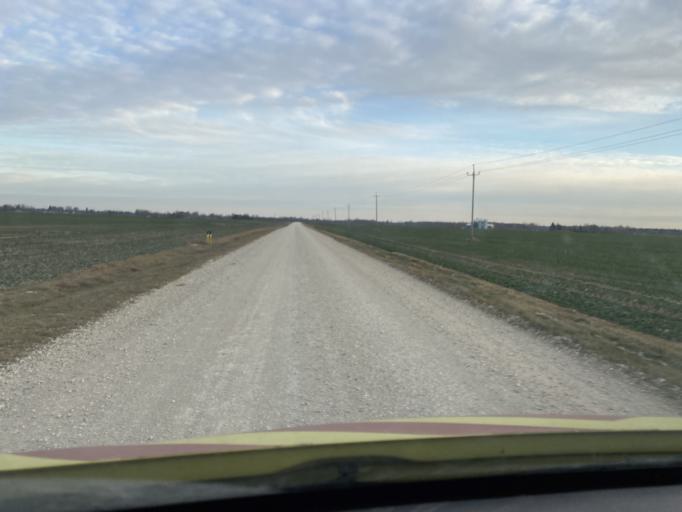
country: EE
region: Jogevamaa
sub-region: Poltsamaa linn
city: Poltsamaa
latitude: 58.5818
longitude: 26.0708
